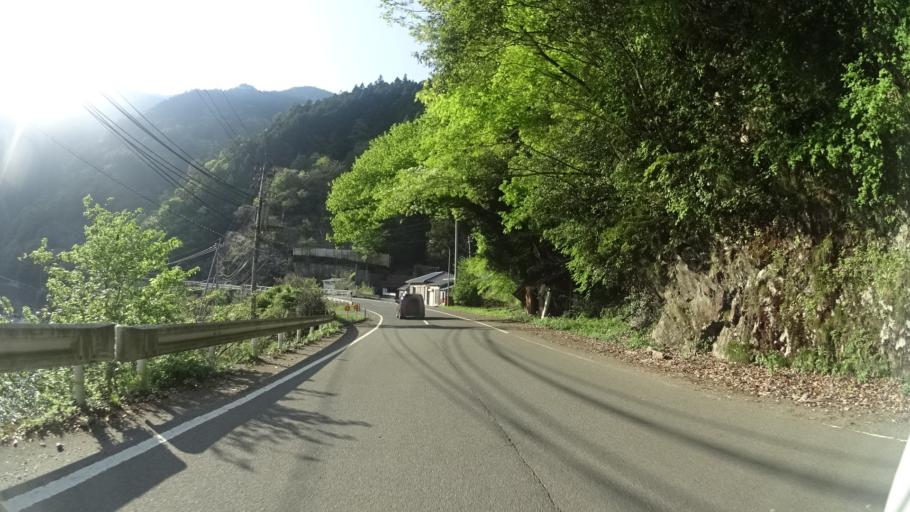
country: JP
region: Tokushima
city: Ikedacho
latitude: 33.8922
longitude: 133.8504
